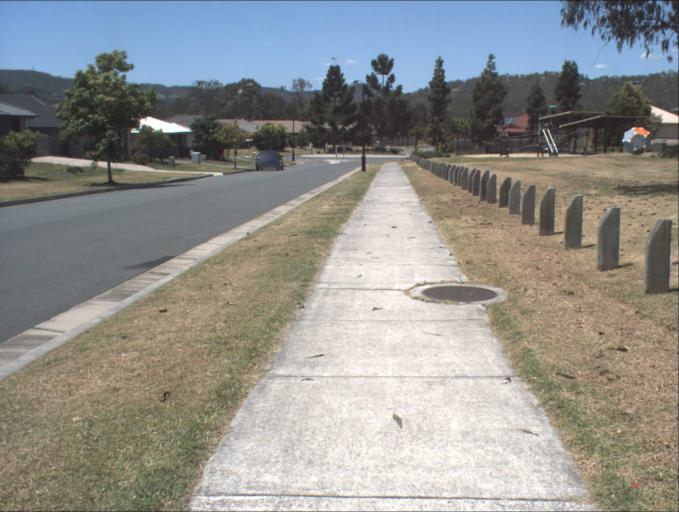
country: AU
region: Queensland
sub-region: Logan
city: Windaroo
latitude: -27.7502
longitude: 153.1849
